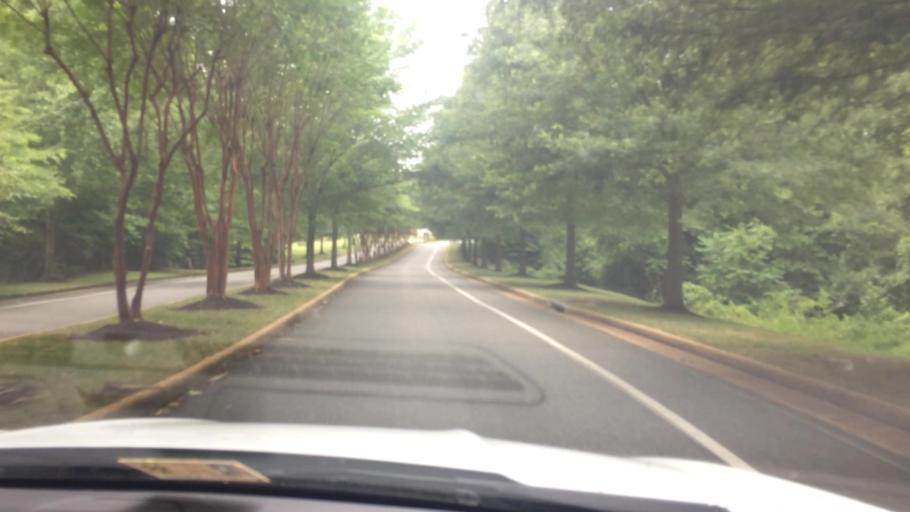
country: US
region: Virginia
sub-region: City of Williamsburg
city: Williamsburg
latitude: 37.2848
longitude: -76.6712
